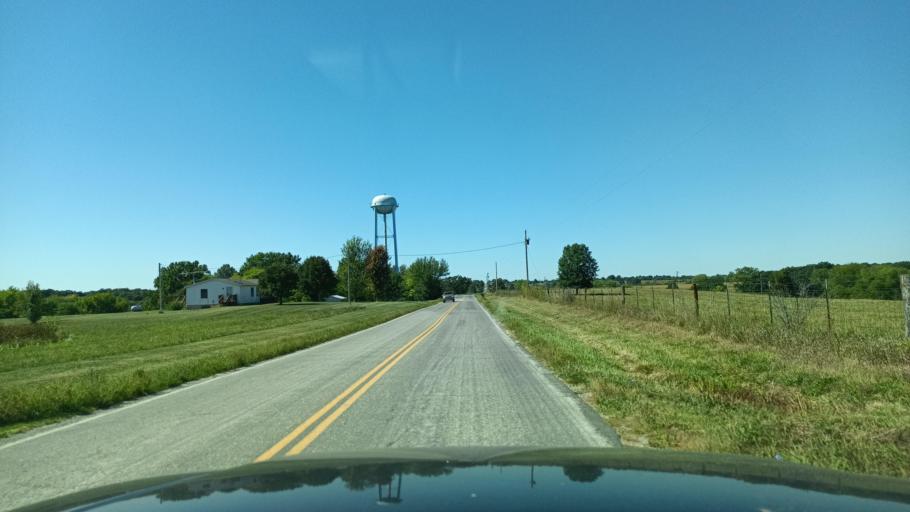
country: US
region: Missouri
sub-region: Macon County
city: La Plata
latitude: 40.0216
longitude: -92.5256
